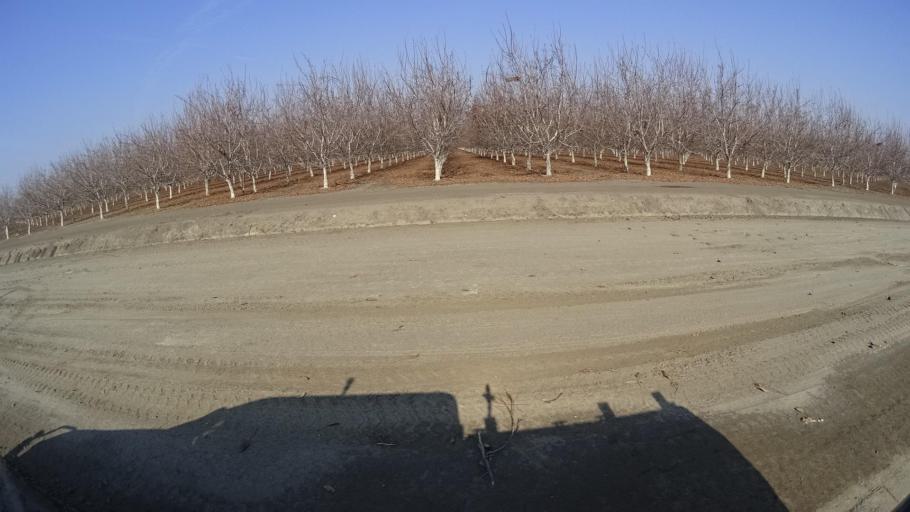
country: US
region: California
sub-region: Kern County
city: Buttonwillow
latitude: 35.3693
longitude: -119.4213
